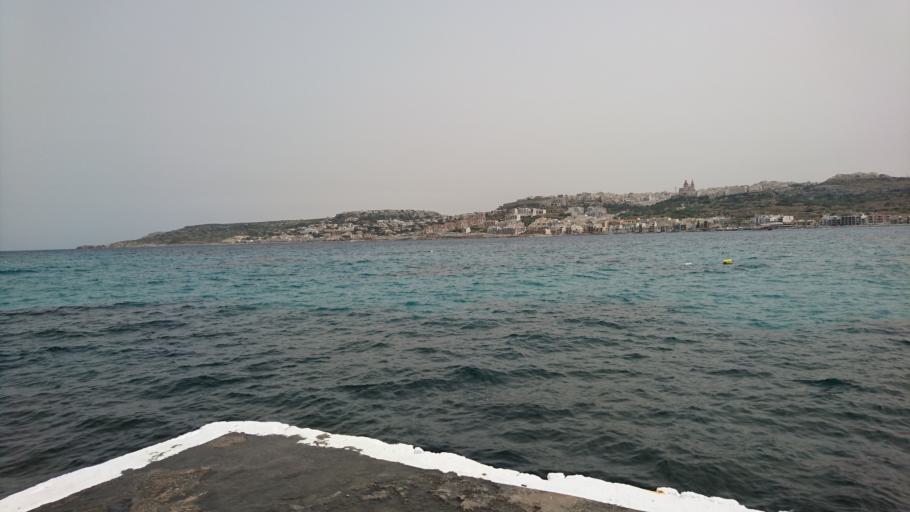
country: MT
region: Il-Mellieha
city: Mellieha
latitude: 35.9749
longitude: 14.3526
